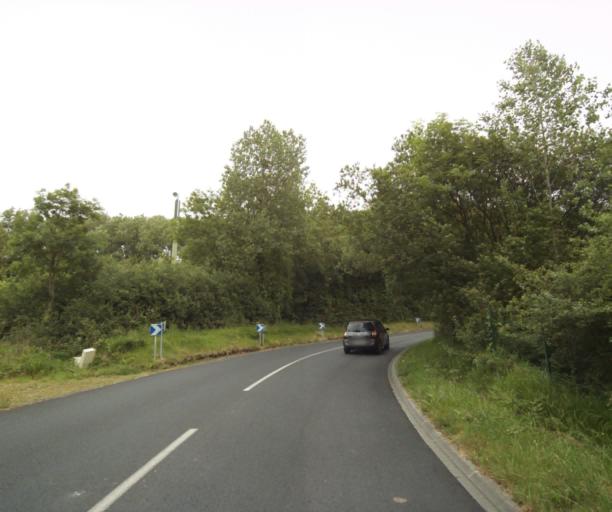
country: FR
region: Lower Normandy
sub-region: Departement du Calvados
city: Houlgate
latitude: 49.2891
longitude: -0.0893
